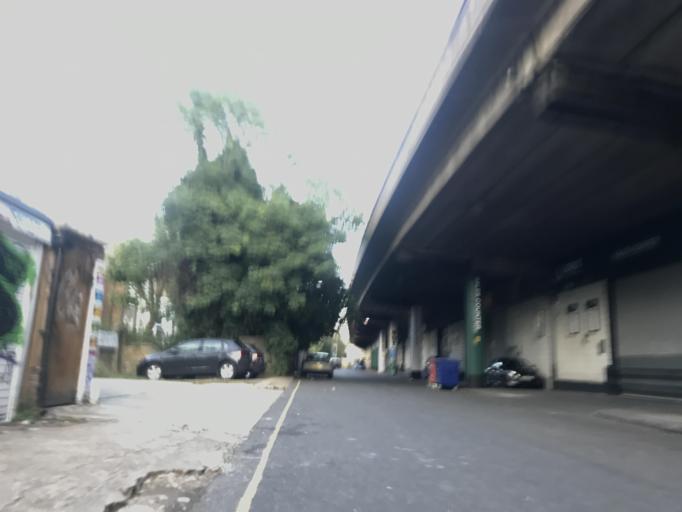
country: GB
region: England
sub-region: Greater London
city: Kensington
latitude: 51.5175
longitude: -0.2128
